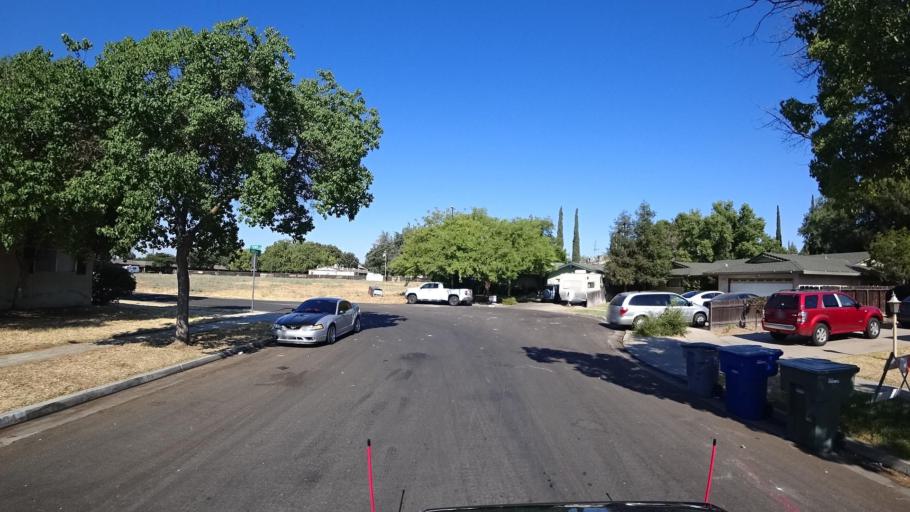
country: US
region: California
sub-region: Fresno County
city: Fresno
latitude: 36.7850
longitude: -119.7700
